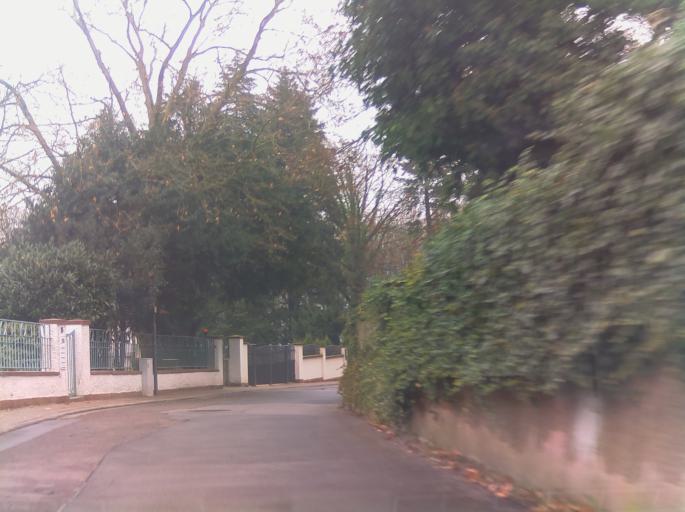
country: DE
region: Baden-Wuerttemberg
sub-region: Karlsruhe Region
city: Heidelberg
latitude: 49.4147
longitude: 8.7253
